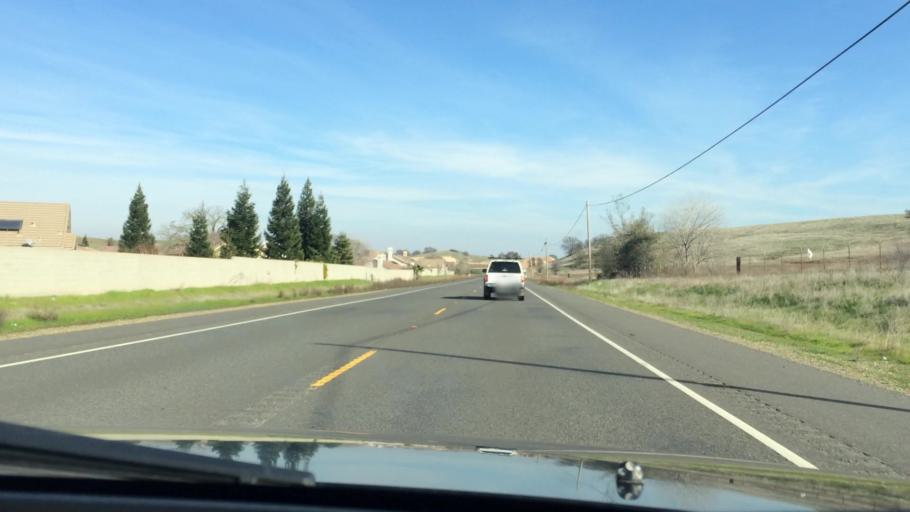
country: US
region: California
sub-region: Sacramento County
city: Rancho Murieta
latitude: 38.4849
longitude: -121.0697
